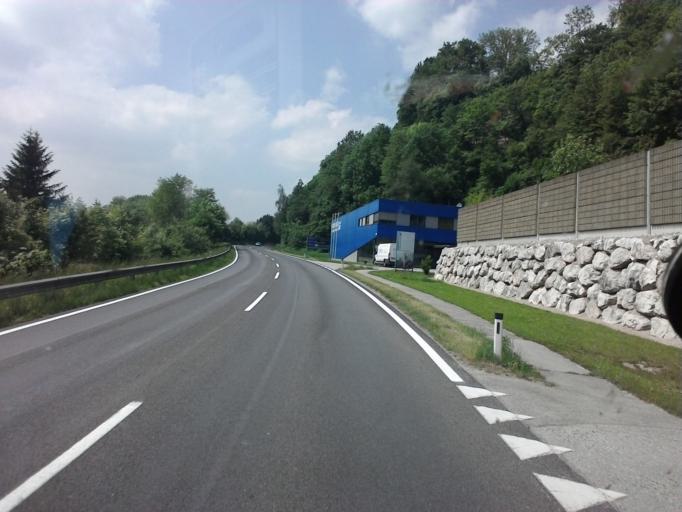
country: AT
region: Upper Austria
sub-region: Politischer Bezirk Steyr-Land
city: Garsten
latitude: 48.0496
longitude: 14.3666
